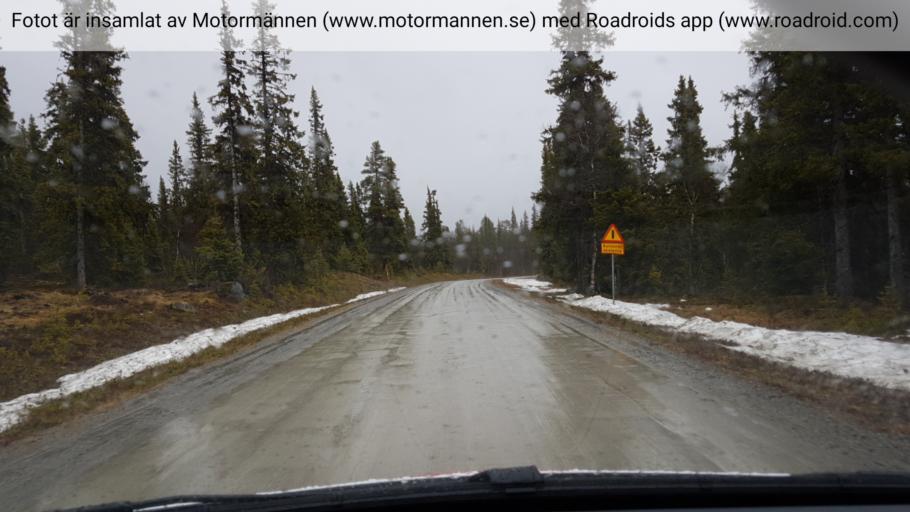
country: SE
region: Jaemtland
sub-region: Are Kommun
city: Are
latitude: 62.6652
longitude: 12.8864
